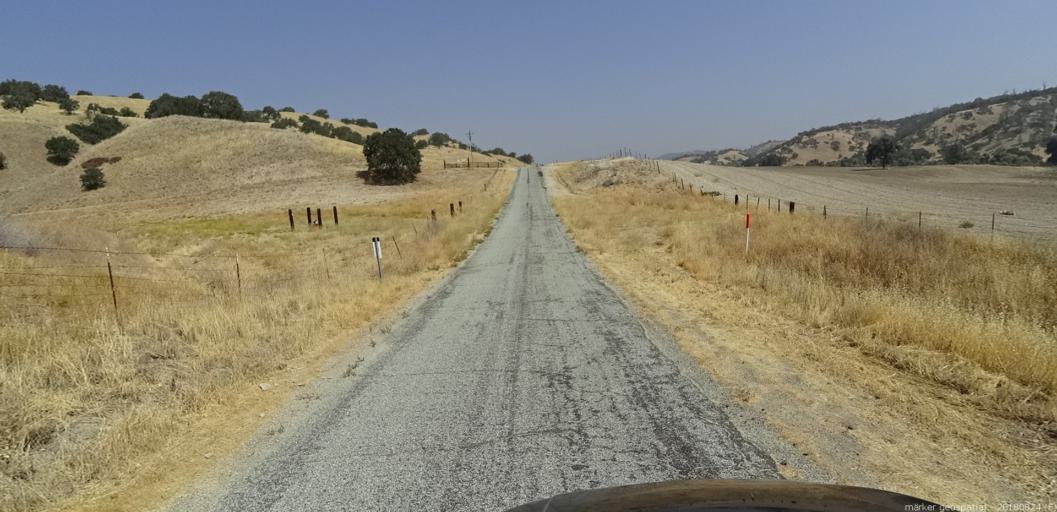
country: US
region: California
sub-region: San Luis Obispo County
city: San Miguel
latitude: 35.9817
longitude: -120.6453
